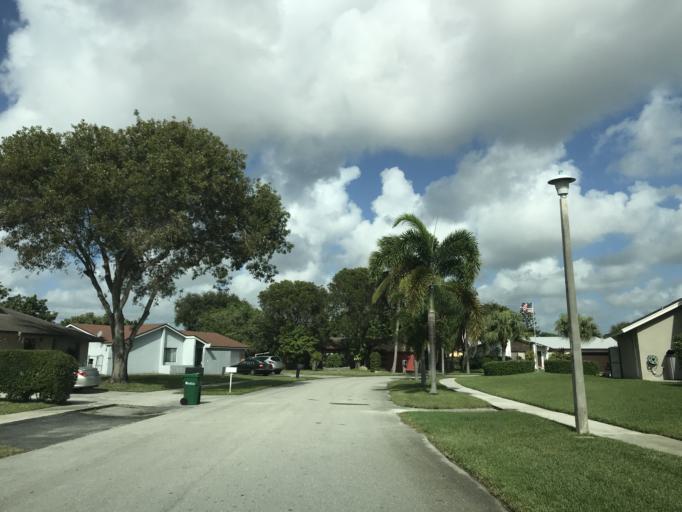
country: US
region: Florida
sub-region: Broward County
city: Coconut Creek
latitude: 26.2627
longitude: -80.1941
